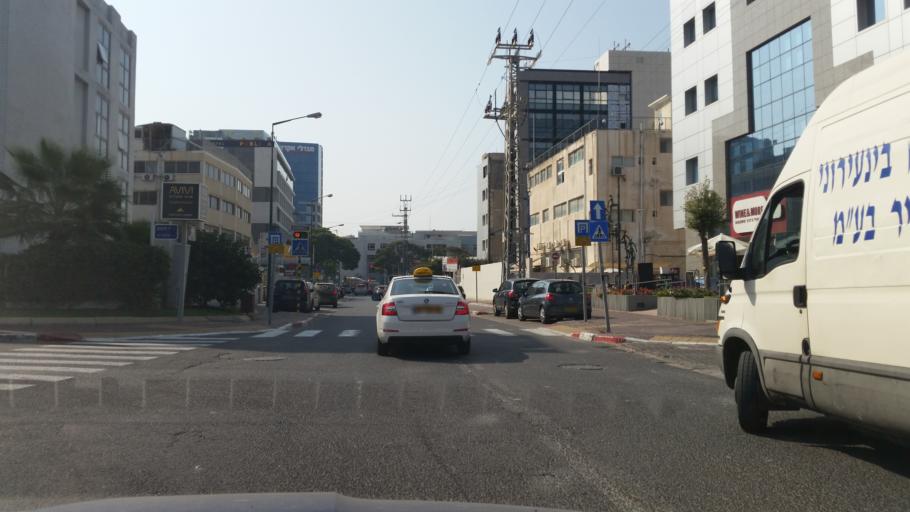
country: IL
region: Tel Aviv
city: Herzliya Pituah
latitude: 32.1639
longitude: 34.8087
